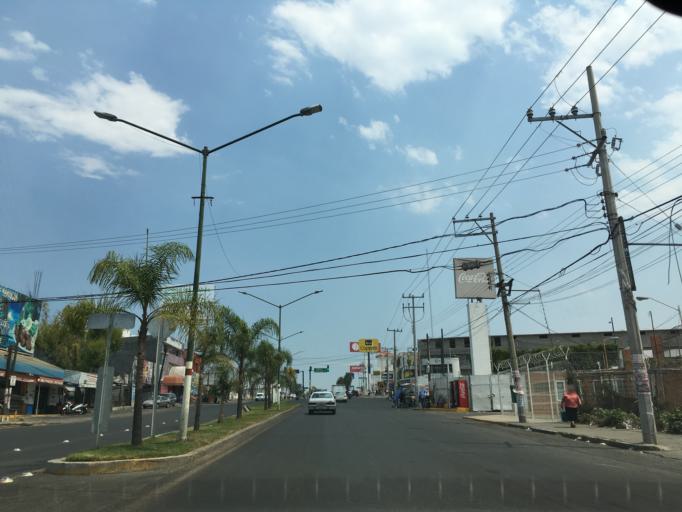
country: MX
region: Guanajuato
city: Moroleon
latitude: 20.1231
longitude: -101.1790
